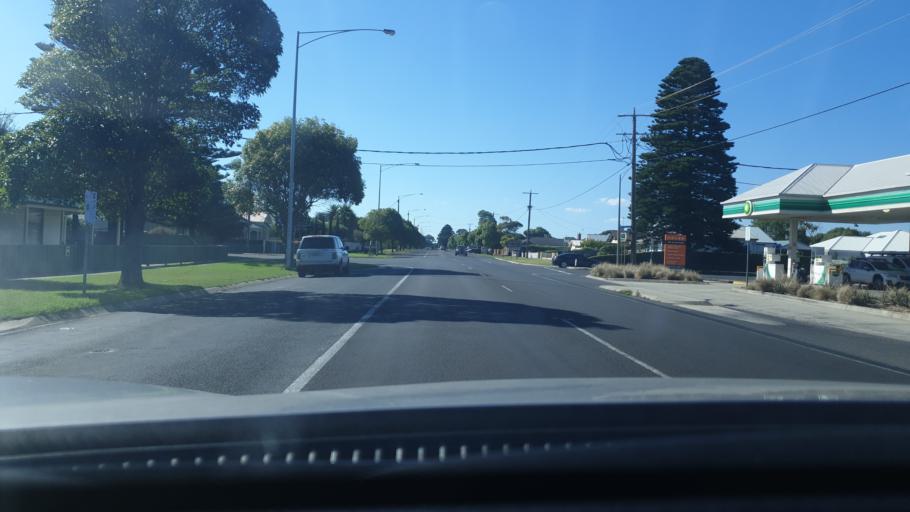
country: AU
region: Victoria
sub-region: Moyne
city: Port Fairy
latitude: -38.3812
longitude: 142.2293
